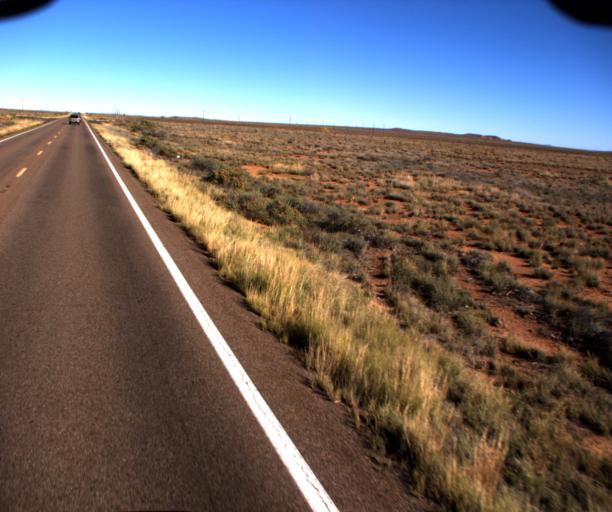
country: US
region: Arizona
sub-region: Navajo County
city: Holbrook
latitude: 34.7869
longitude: -110.1317
